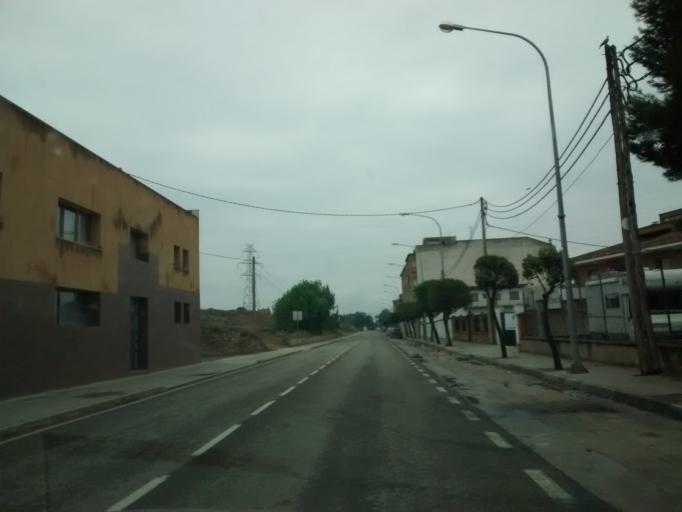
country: ES
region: Aragon
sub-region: Provincia de Zaragoza
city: Caspe
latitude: 41.2288
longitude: -0.0362
